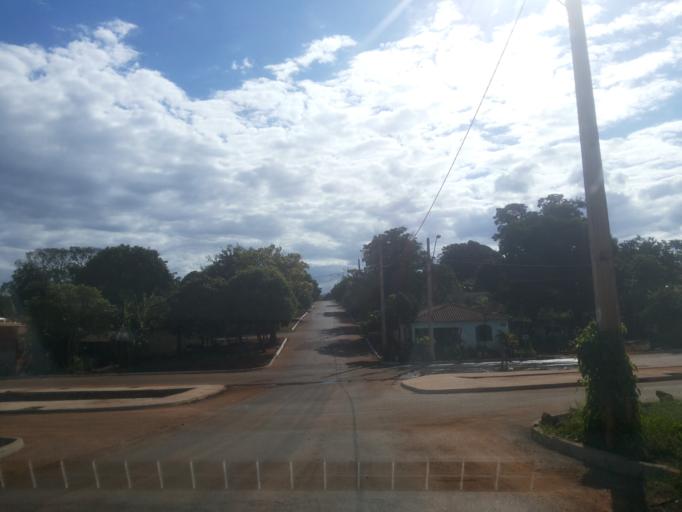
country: BR
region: Goias
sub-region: Itumbiara
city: Itumbiara
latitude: -18.4373
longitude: -49.1880
